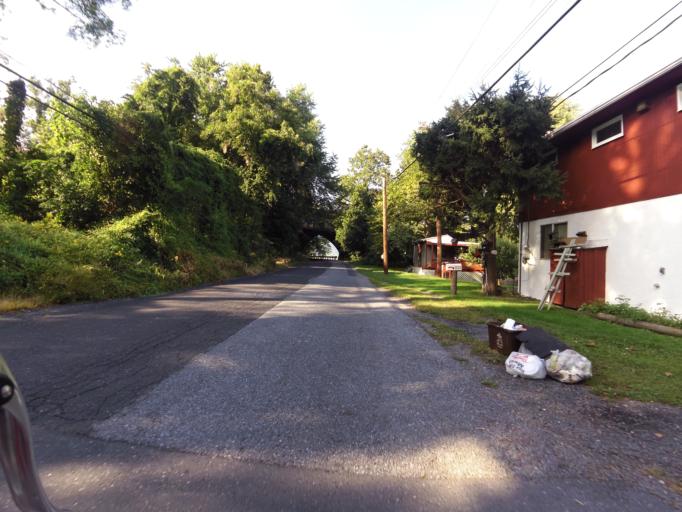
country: US
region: Pennsylvania
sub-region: Perry County
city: Marysville
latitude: 40.3307
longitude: -76.9169
